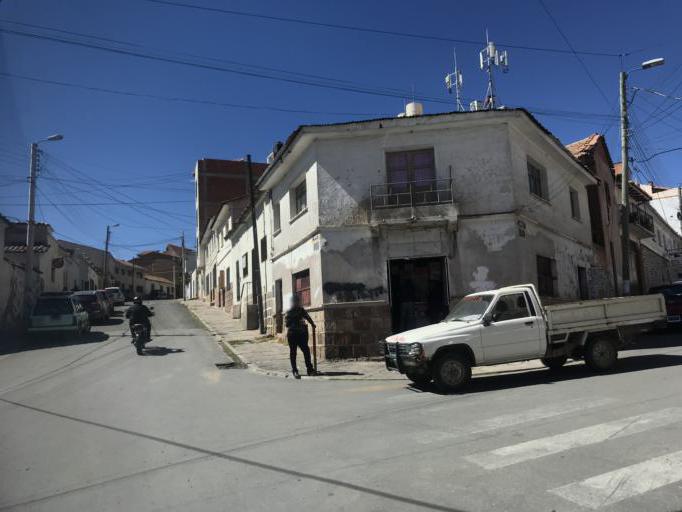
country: BO
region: Chuquisaca
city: Sucre
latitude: -19.0415
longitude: -65.2565
